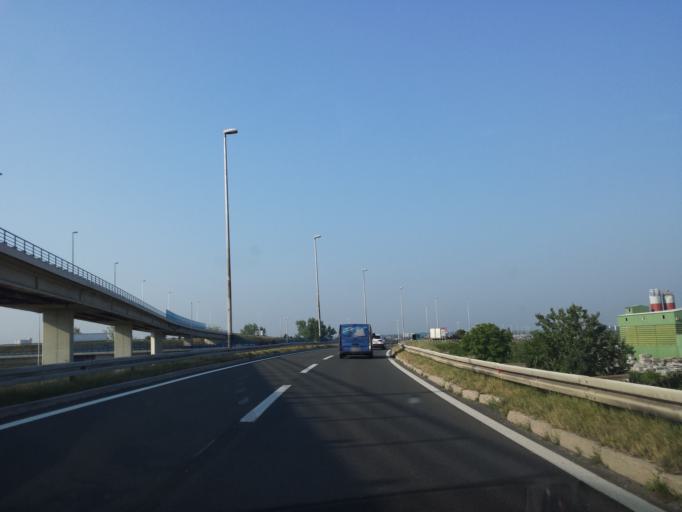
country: HR
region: Grad Zagreb
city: Lucko
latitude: 45.7591
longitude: 15.8967
